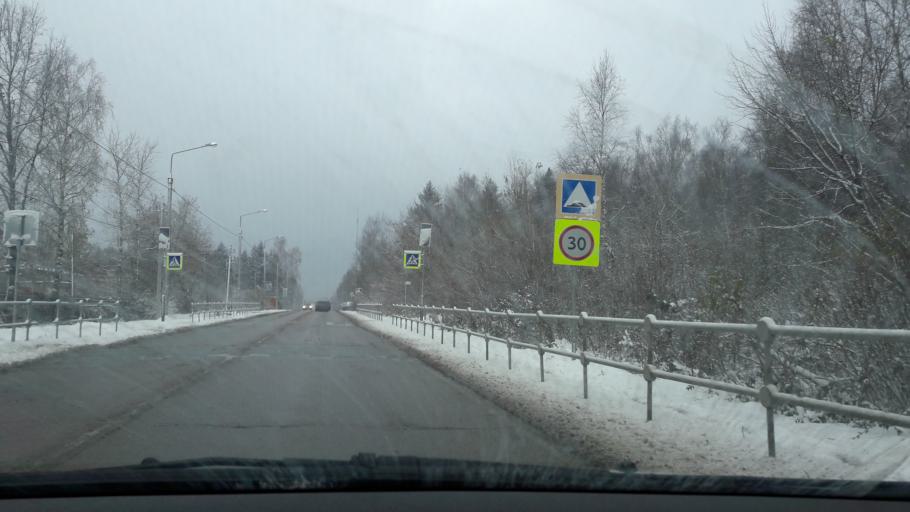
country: RU
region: Moskovskaya
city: Zvenigorod
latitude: 55.6257
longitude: 36.8664
